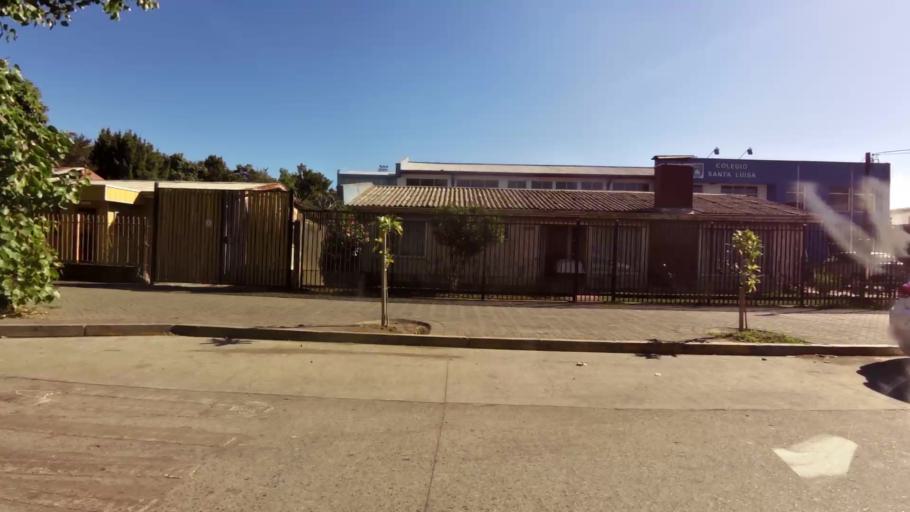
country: CL
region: Biobio
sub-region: Provincia de Concepcion
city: Concepcion
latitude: -36.8126
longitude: -73.0733
